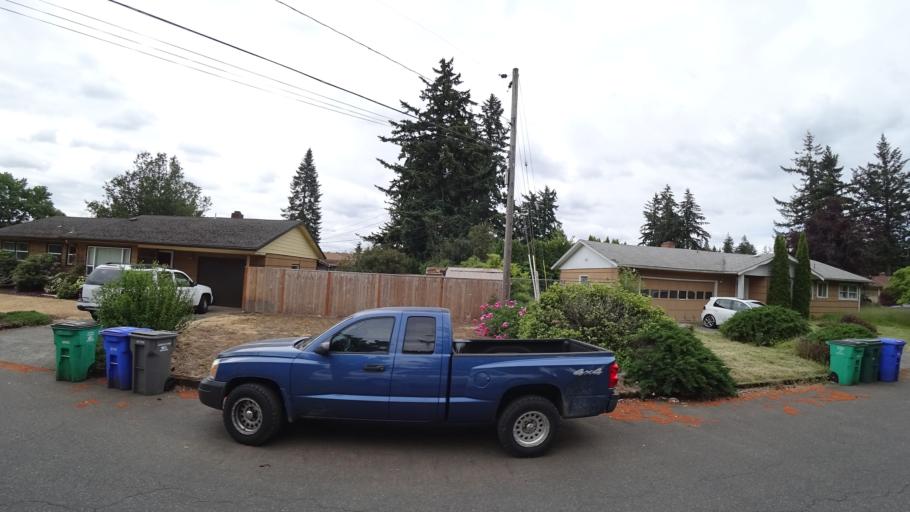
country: US
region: Oregon
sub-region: Multnomah County
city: Lents
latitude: 45.5023
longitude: -122.5392
